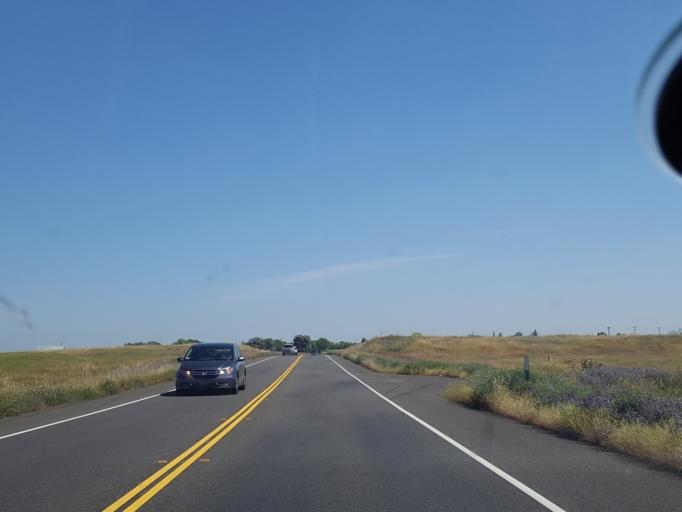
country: US
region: California
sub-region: Sacramento County
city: Rancho Cordova
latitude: 38.5658
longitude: -121.2656
